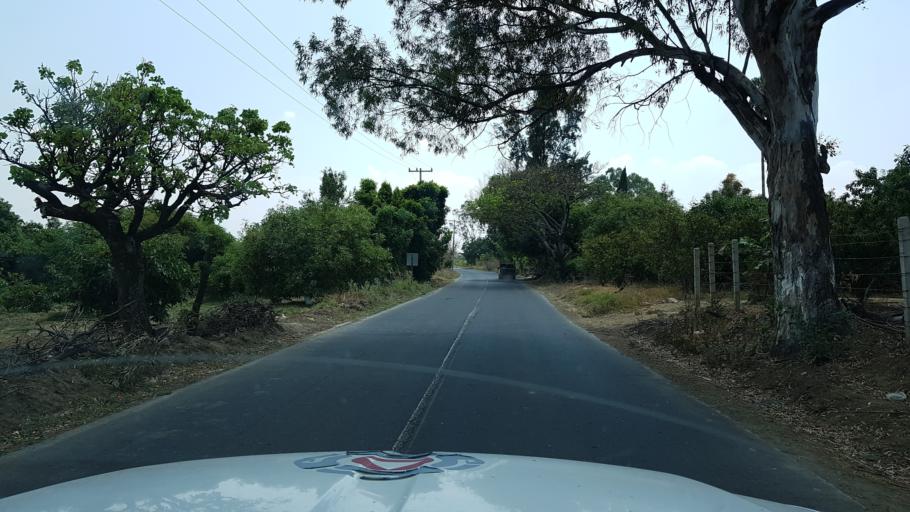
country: MX
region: Morelos
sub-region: Yecapixtla
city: Texcala
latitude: 18.9313
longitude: -98.8063
